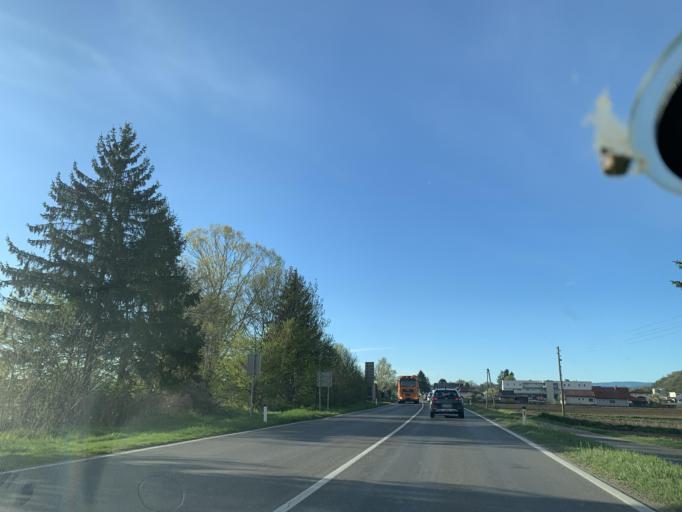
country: AT
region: Styria
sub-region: Politischer Bezirk Leibnitz
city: Kaindorf an der Sulm
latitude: 46.8120
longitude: 15.5270
